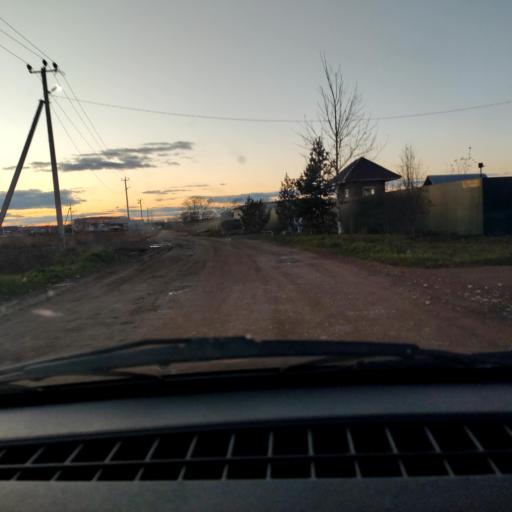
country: RU
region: Bashkortostan
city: Ufa
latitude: 54.6444
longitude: 55.9146
